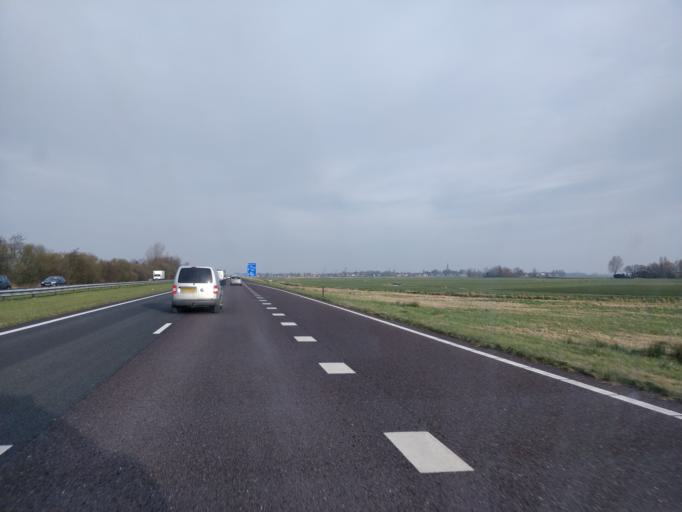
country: NL
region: Friesland
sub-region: Gemeente Leeuwarden
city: Wirdum
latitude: 53.1334
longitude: 5.8017
